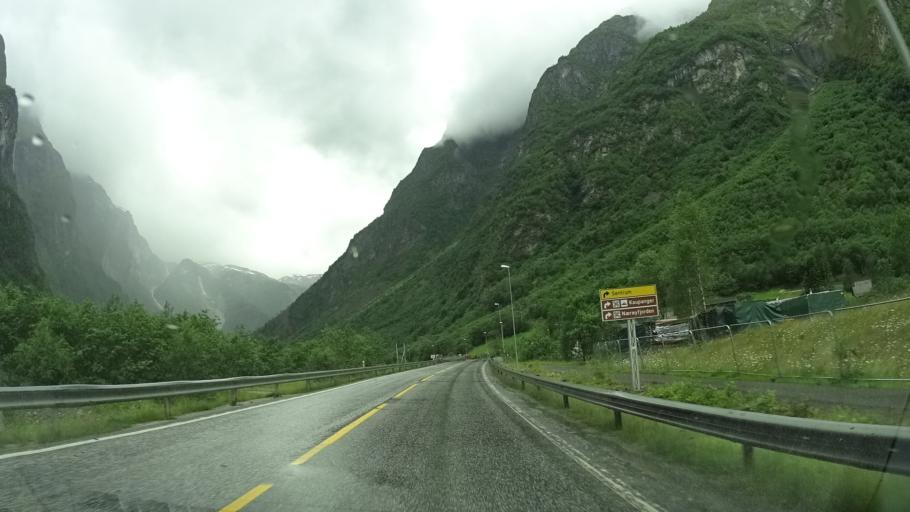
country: NO
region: Sogn og Fjordane
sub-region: Leikanger
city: Hermansverk
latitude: 60.8787
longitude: 6.8424
